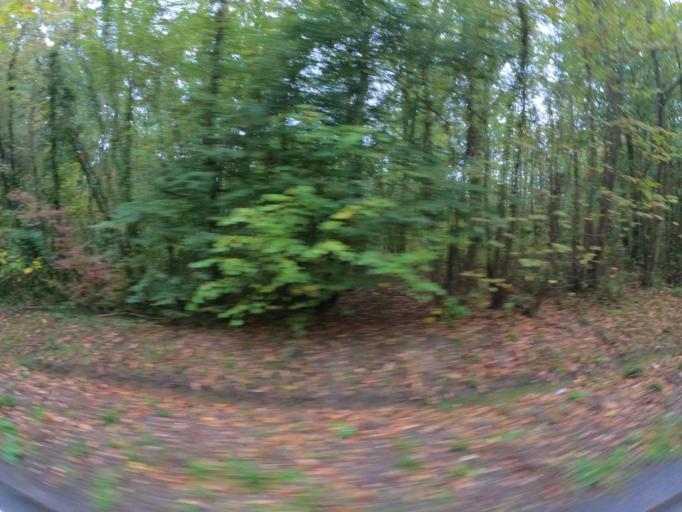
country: FR
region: Ile-de-France
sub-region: Departement de Seine-et-Marne
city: Serris
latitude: 48.8236
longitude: 2.7714
